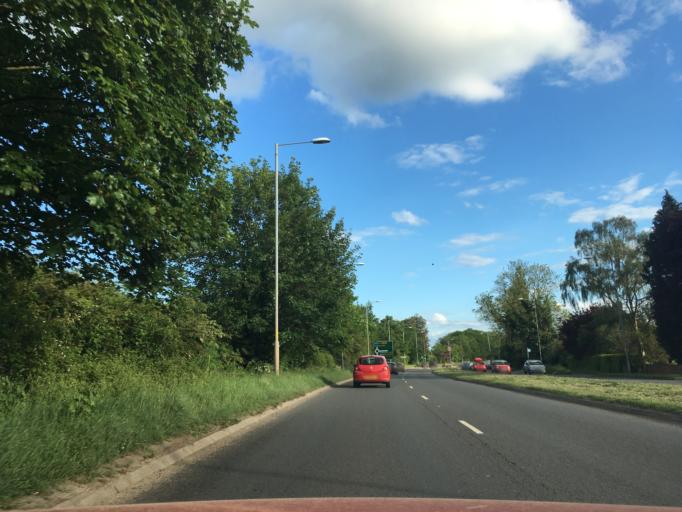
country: GB
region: England
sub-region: Worcestershire
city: Worcester
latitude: 52.1757
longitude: -2.1849
